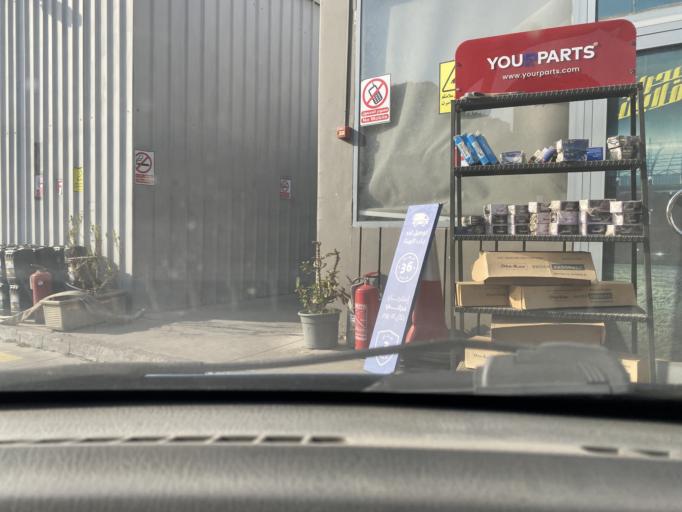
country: EG
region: Muhafazat al Qahirah
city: Cairo
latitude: 30.1033
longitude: 31.3019
